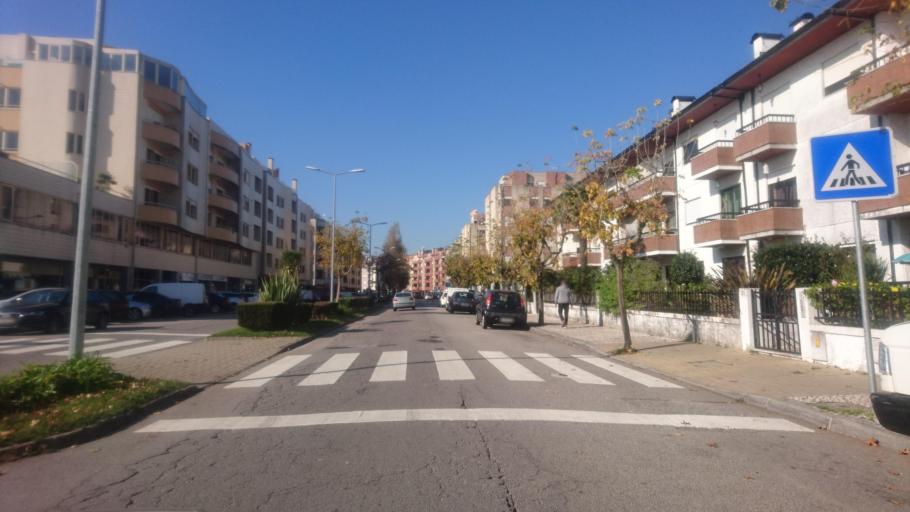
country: PT
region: Aveiro
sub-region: Santa Maria da Feira
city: Feira
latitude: 40.9243
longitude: -8.5607
